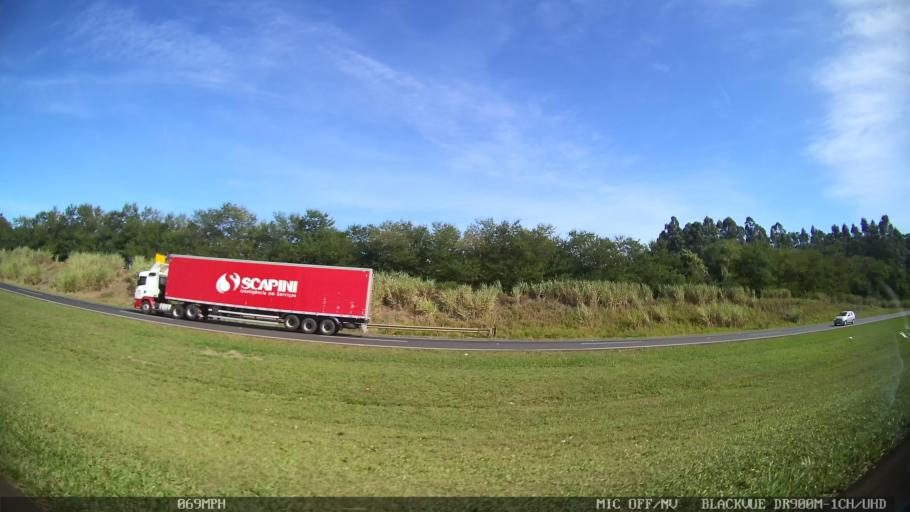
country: BR
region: Sao Paulo
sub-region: Leme
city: Leme
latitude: -22.2323
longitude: -47.3912
